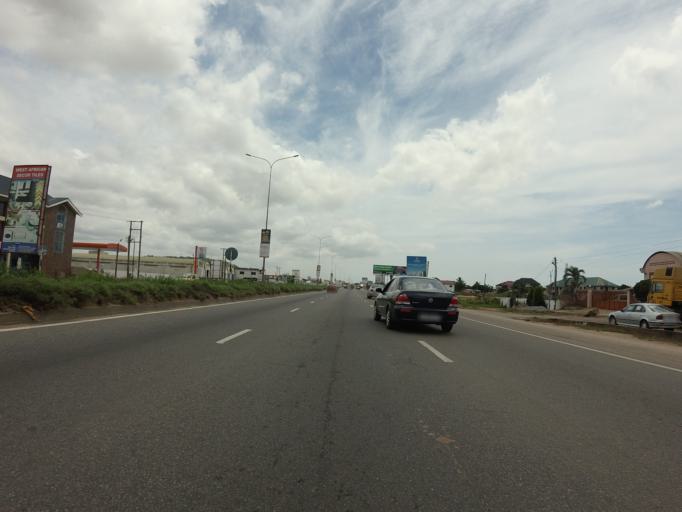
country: GH
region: Greater Accra
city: Gbawe
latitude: 5.5532
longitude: -0.3212
